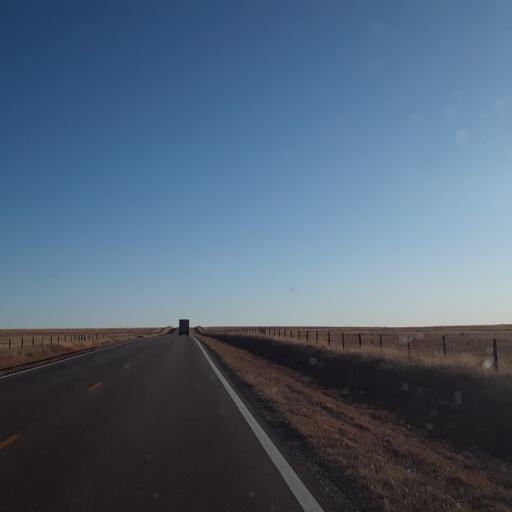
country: US
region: Kansas
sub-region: Wallace County
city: Sharon Springs
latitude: 39.0297
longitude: -101.7386
